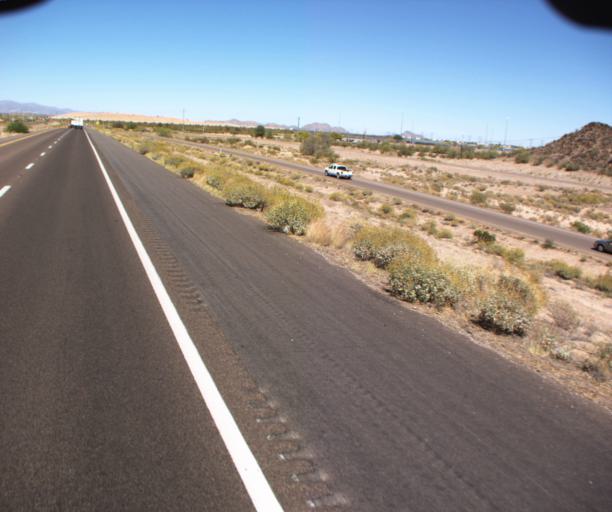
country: US
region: Arizona
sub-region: Maricopa County
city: Buckeye
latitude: 33.1975
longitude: -112.6496
